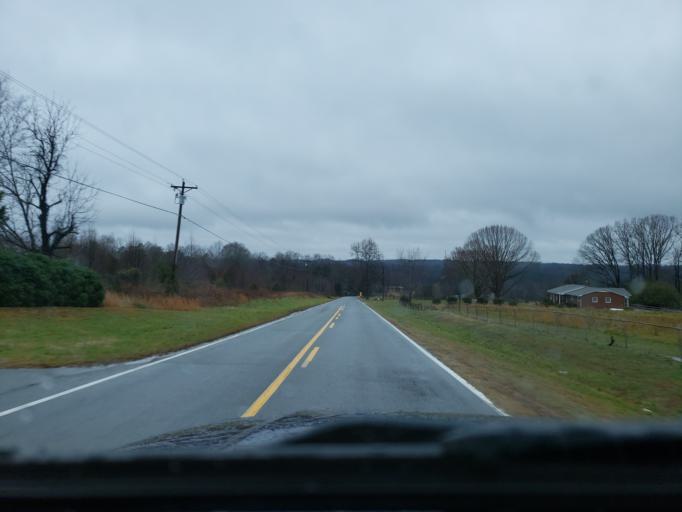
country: US
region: North Carolina
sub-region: Cleveland County
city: White Plains
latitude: 35.1767
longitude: -81.3653
